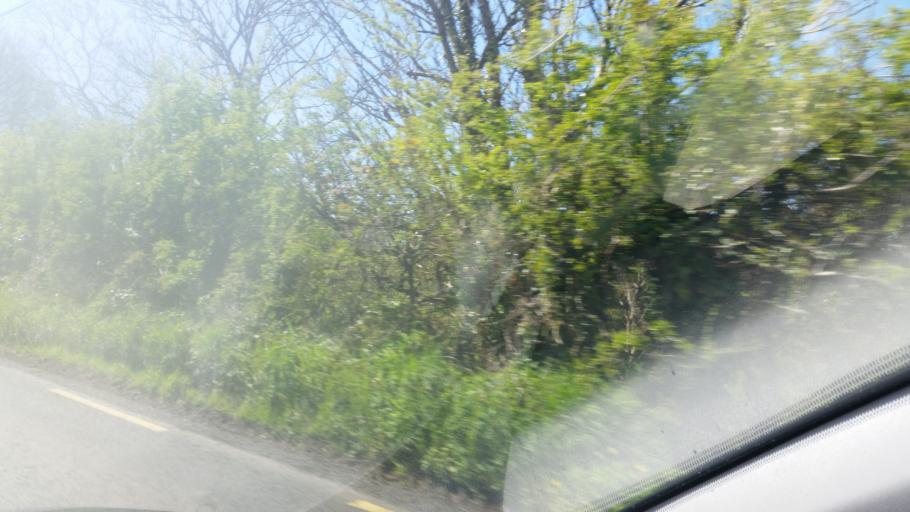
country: IE
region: Munster
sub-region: Waterford
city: Dunmore East
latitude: 52.2111
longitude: -6.8594
